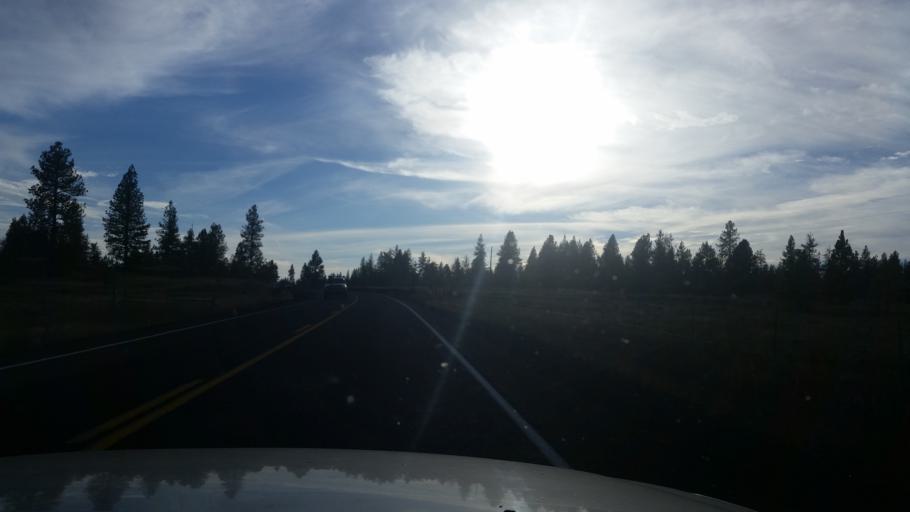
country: US
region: Washington
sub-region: Spokane County
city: Cheney
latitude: 47.3832
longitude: -117.5827
